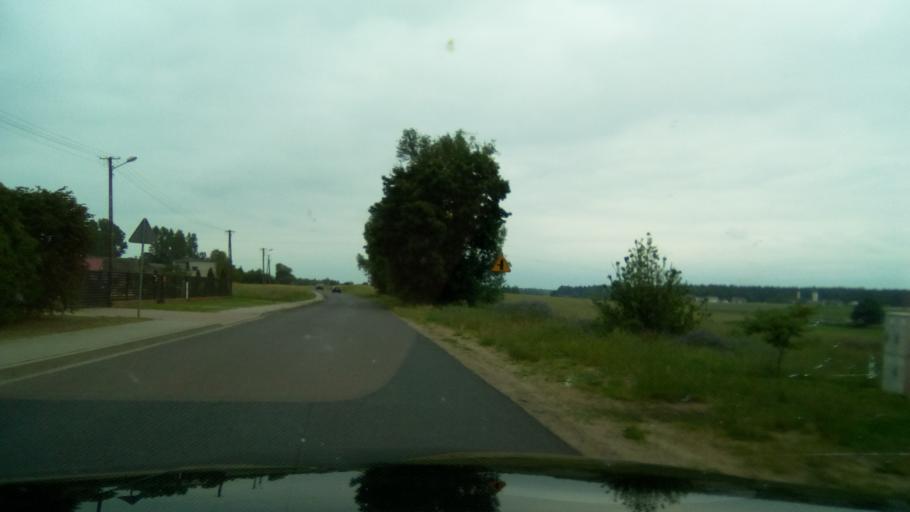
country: PL
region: Greater Poland Voivodeship
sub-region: Powiat gnieznienski
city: Czerniejewo
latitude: 52.4788
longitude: 17.5160
